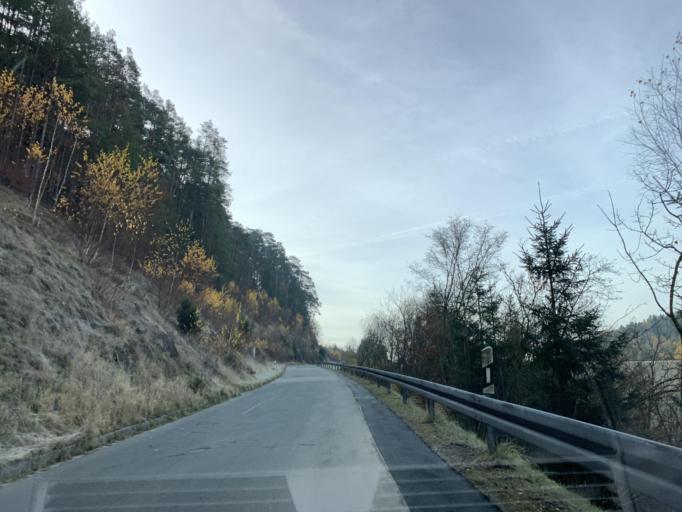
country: DE
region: Bavaria
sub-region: Upper Palatinate
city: Thanstein
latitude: 49.3589
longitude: 12.4487
